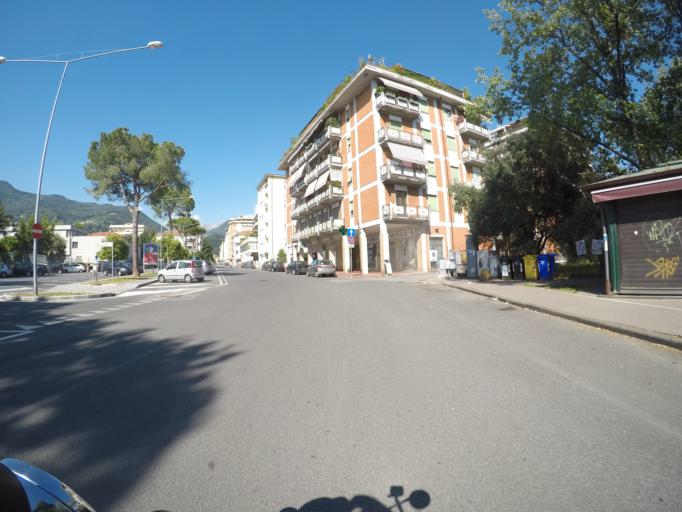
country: IT
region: Tuscany
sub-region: Provincia di Massa-Carrara
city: Massa
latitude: 44.0343
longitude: 10.1343
